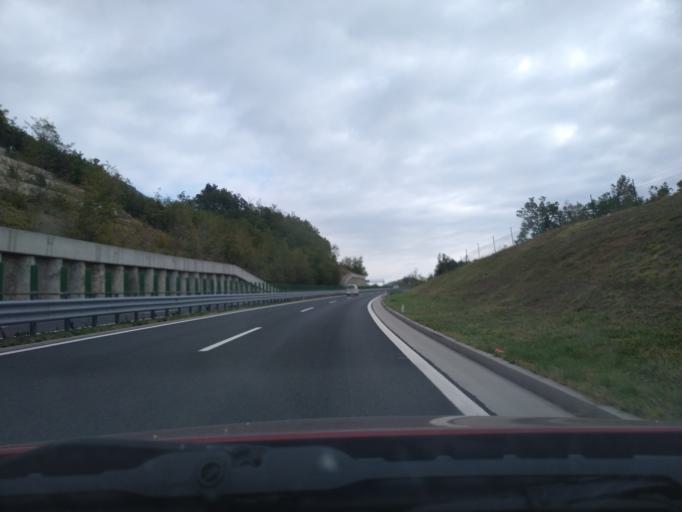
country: SI
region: Vipava
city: Vipava
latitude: 45.7831
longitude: 14.0102
